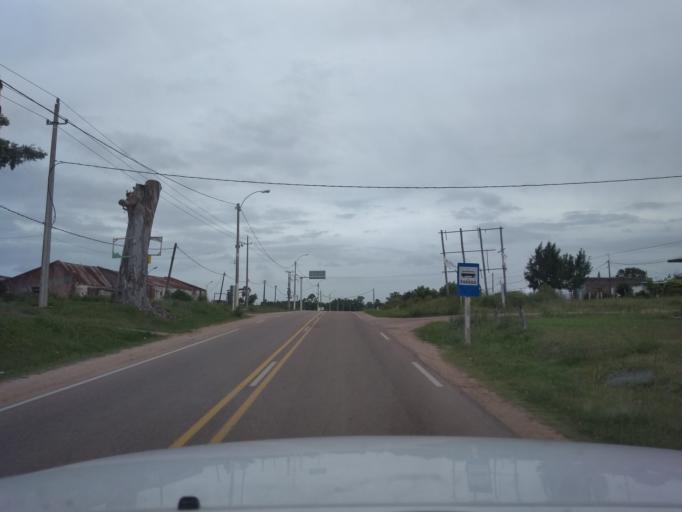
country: UY
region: Canelones
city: Tala
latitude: -34.3500
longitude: -55.7675
